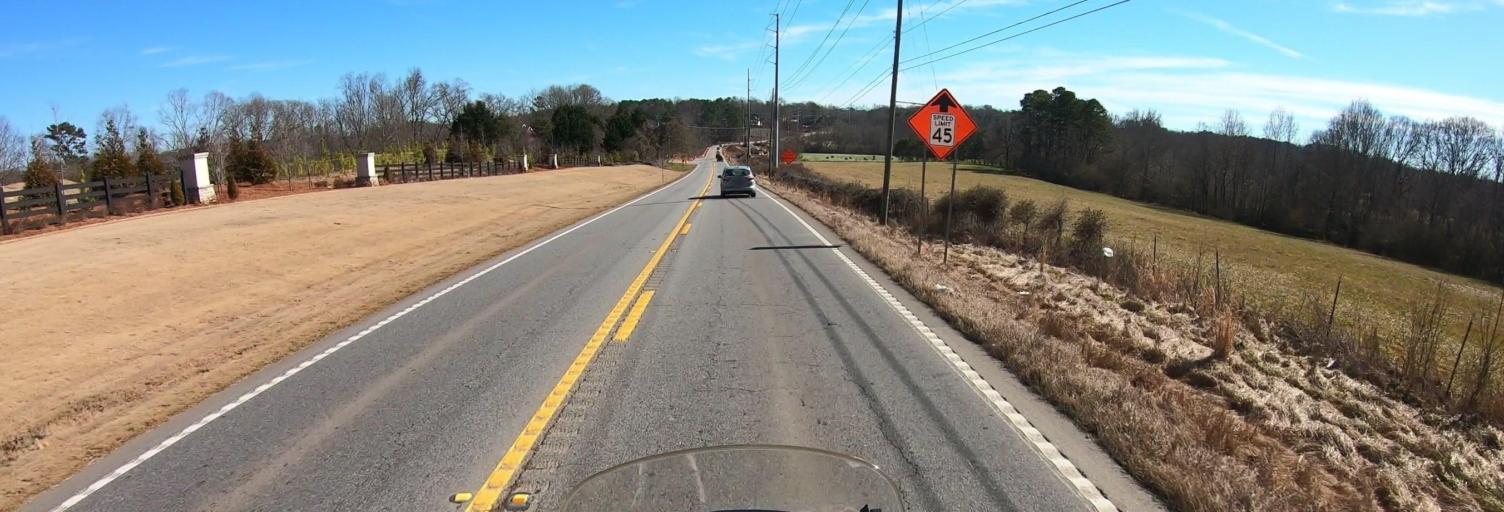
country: US
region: Georgia
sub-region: Forsyth County
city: Cumming
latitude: 34.2911
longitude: -84.1478
